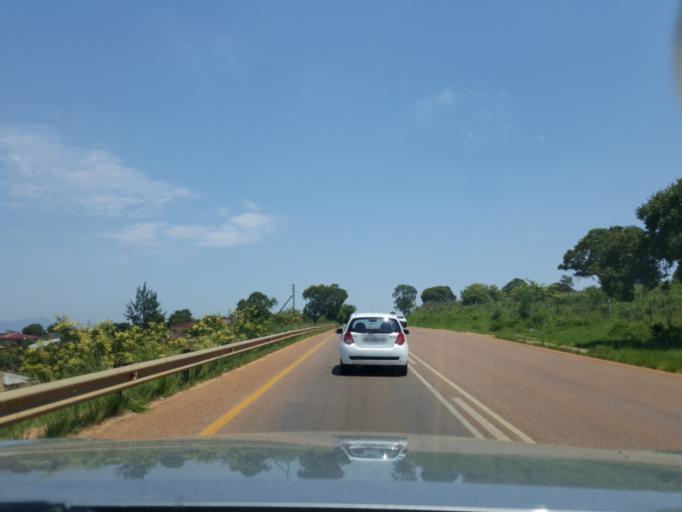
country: ZA
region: Limpopo
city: Thulamahashi
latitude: -24.9173
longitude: 31.1207
